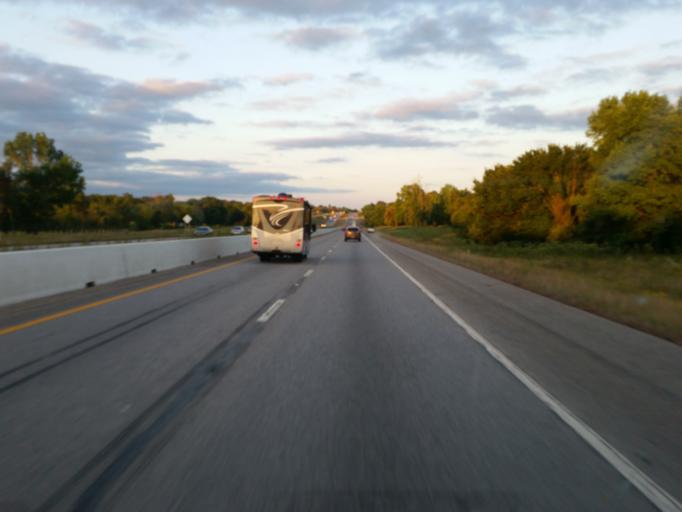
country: US
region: Texas
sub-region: Van Zandt County
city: Van
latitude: 32.4998
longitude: -95.6031
